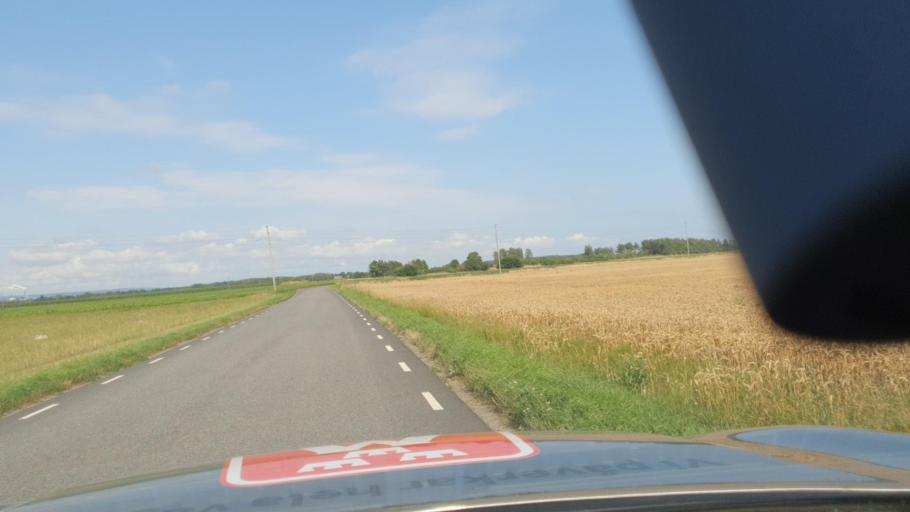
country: SE
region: Skane
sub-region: Bromolla Kommun
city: Bromoella
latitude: 56.0138
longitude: 14.4060
